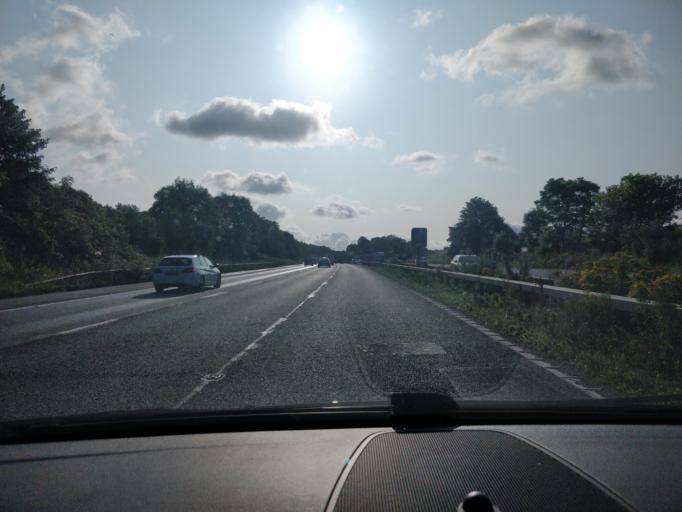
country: GB
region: England
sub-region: Knowsley
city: Huyton
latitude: 53.4303
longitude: -2.8378
